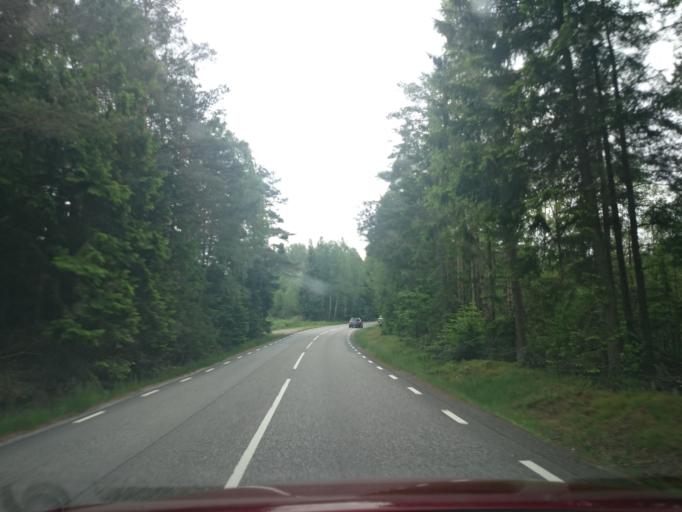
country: SE
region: Vaestra Goetaland
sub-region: Harryda Kommun
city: Hindas
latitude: 57.7069
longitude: 12.3520
